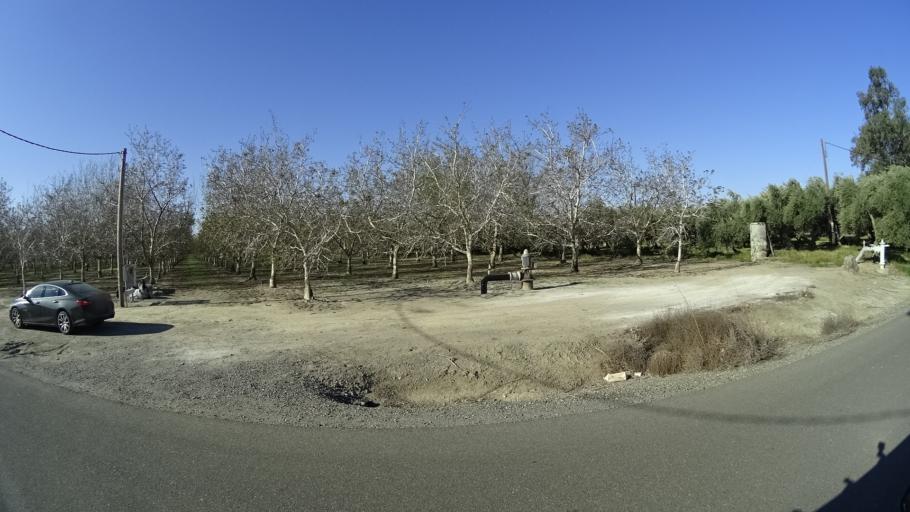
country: US
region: California
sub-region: Glenn County
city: Orland
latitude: 39.7212
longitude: -122.1749
